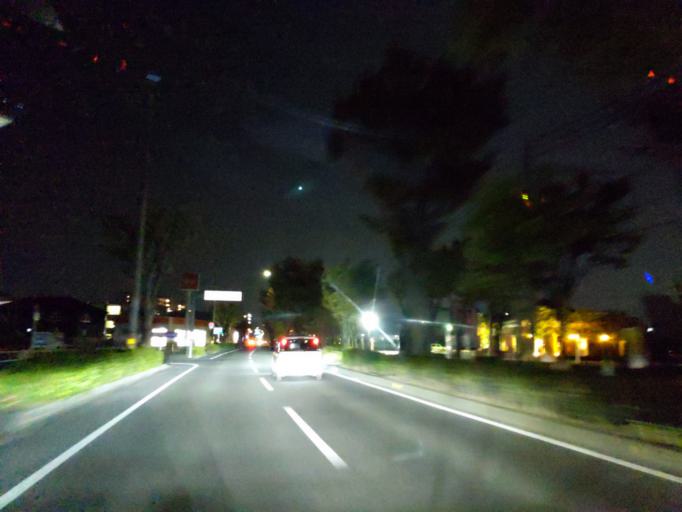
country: JP
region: Okayama
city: Okayama-shi
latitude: 34.6755
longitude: 133.9443
